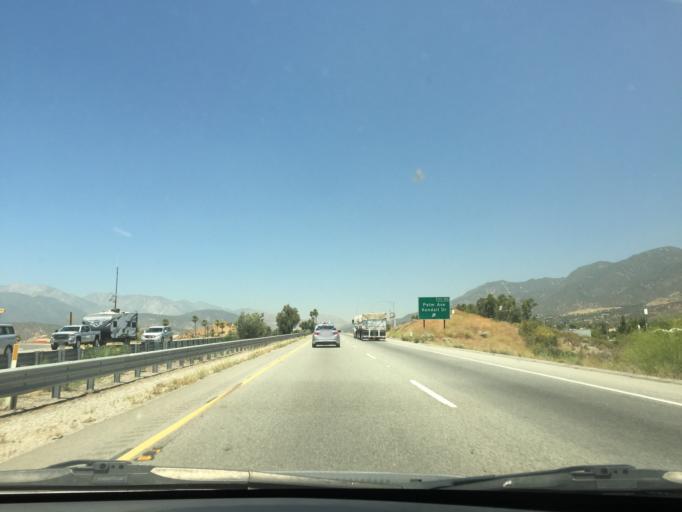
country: US
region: California
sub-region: San Bernardino County
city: Muscoy
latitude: 34.1888
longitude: -117.3580
